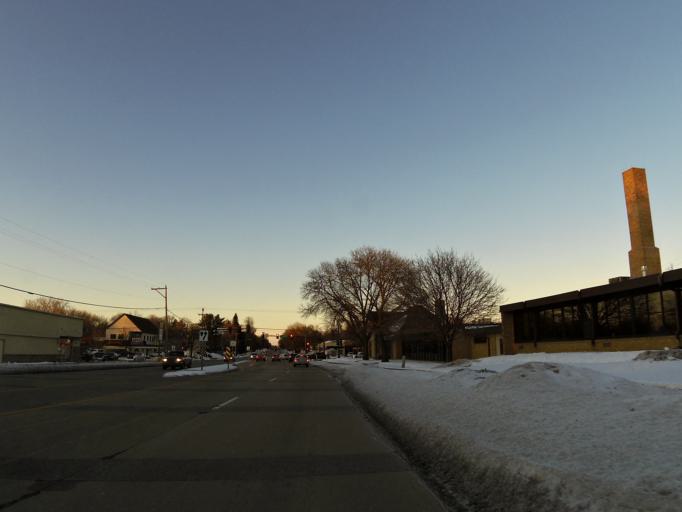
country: US
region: Minnesota
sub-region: Ramsey County
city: White Bear Lake
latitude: 45.0492
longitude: -93.0153
